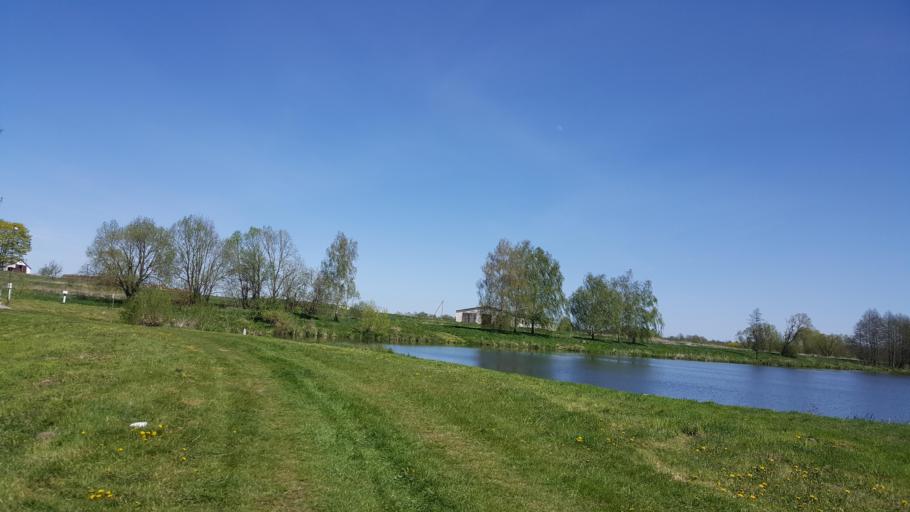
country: BY
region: Brest
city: Kamyanyets
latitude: 52.4368
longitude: 23.8474
